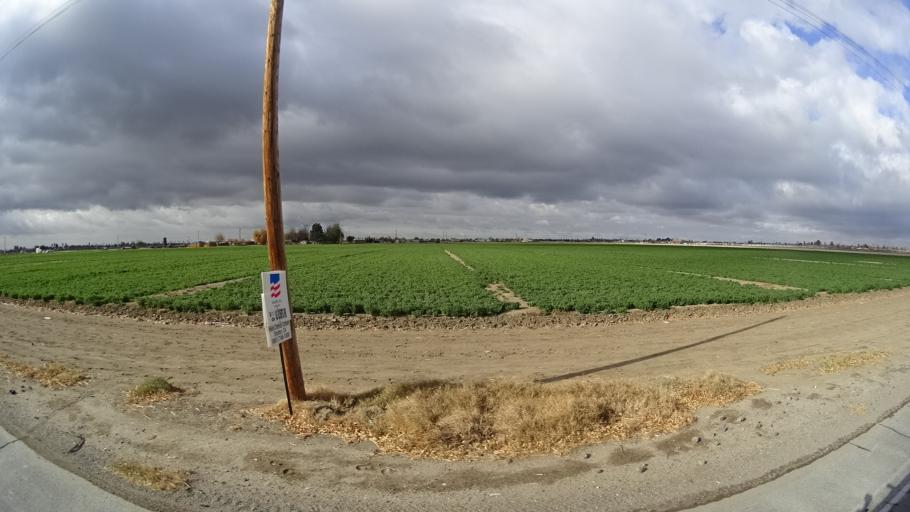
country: US
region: California
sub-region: Kern County
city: Greenfield
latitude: 35.2887
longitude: -118.9853
